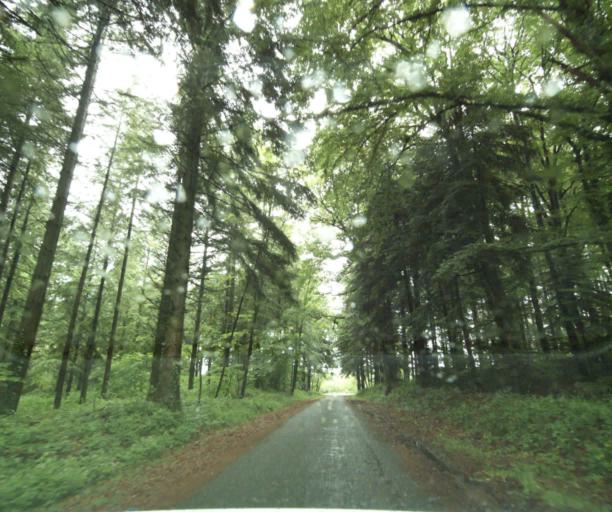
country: FR
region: Bourgogne
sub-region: Departement de Saone-et-Loire
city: Charolles
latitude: 46.4783
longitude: 4.4139
